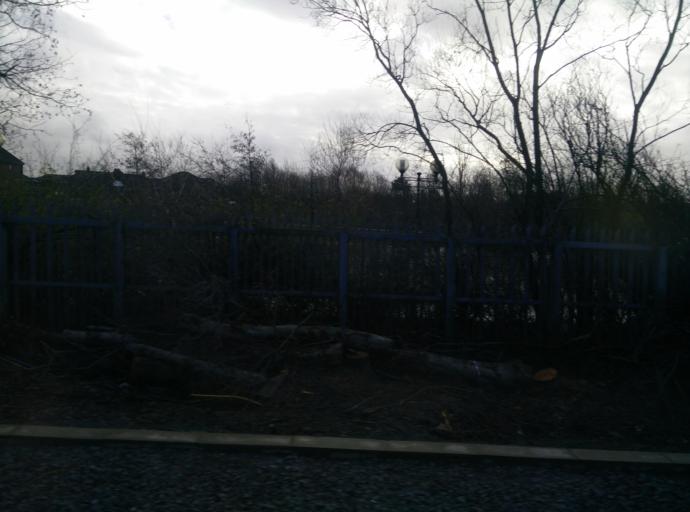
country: GB
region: Northern Ireland
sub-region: City of Belfast
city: Belfast
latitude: 54.5924
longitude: -5.9189
